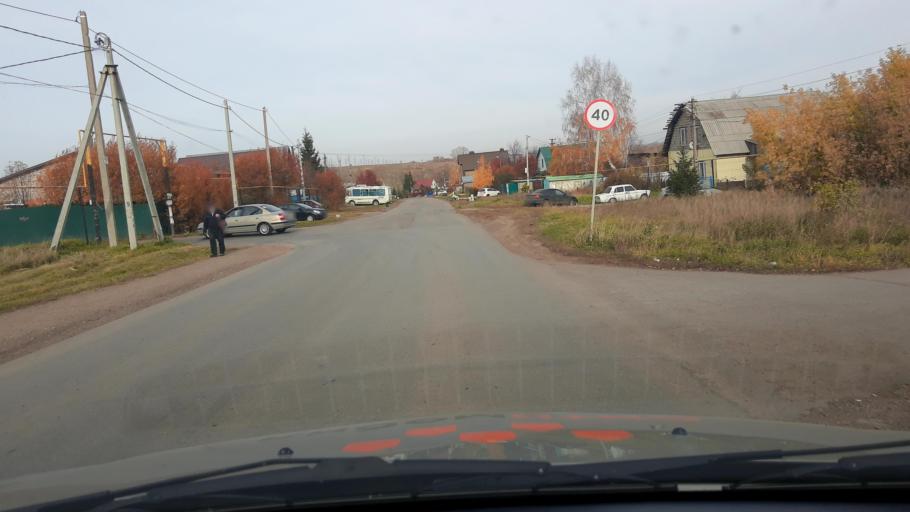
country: RU
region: Bashkortostan
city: Avdon
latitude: 54.7031
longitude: 55.8077
